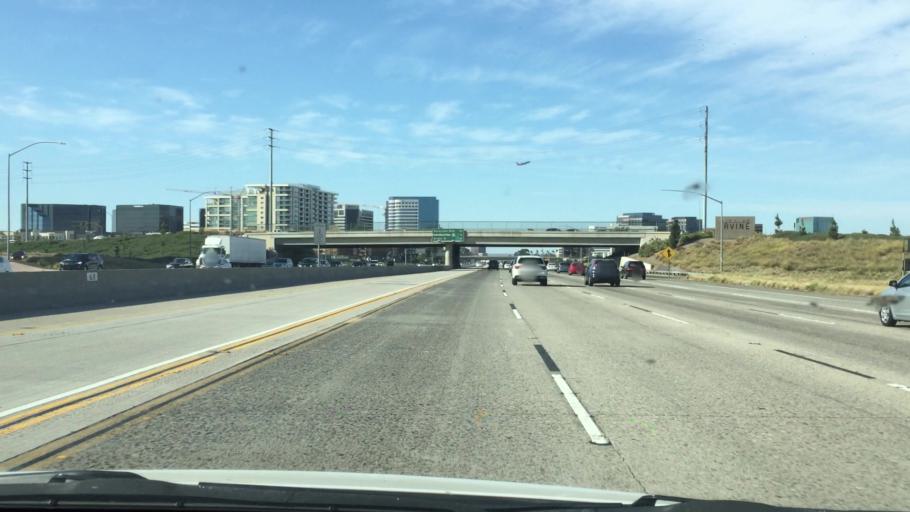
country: US
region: California
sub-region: Orange County
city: Irvine
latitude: 33.6760
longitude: -117.8416
